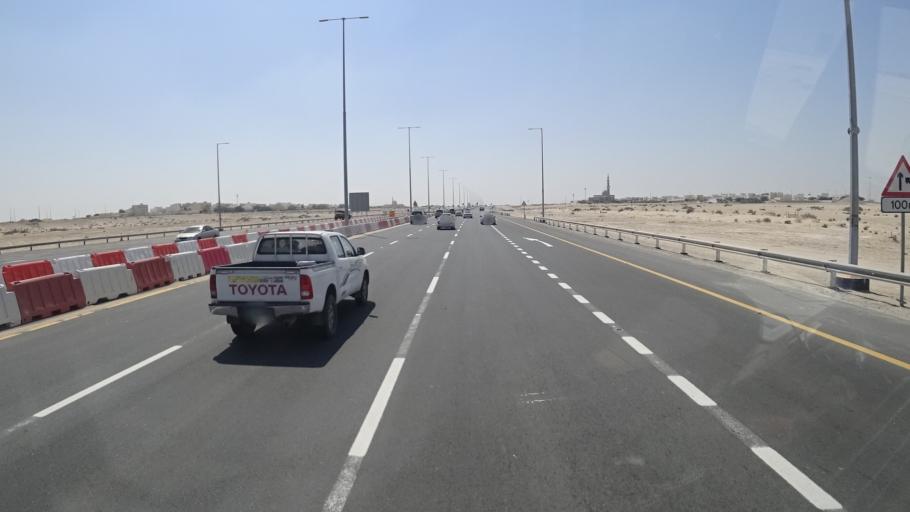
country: AE
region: Abu Dhabi
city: Abu Dhabi
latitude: 24.3366
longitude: 54.6986
